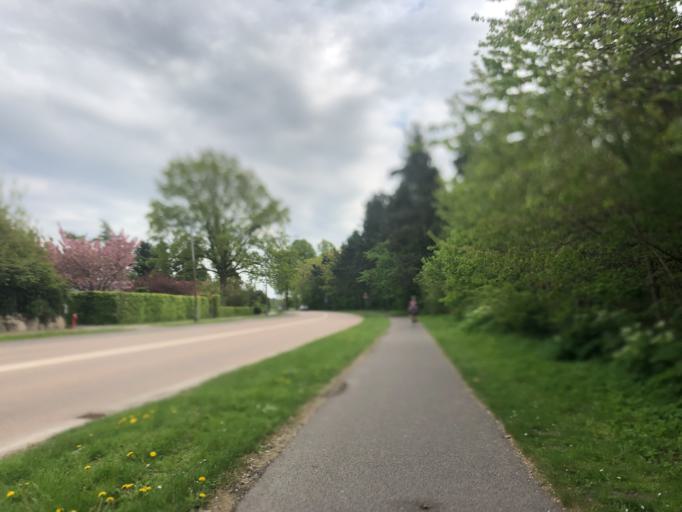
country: DK
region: Zealand
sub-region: Koge Kommune
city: Koge
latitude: 55.4625
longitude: 12.1715
